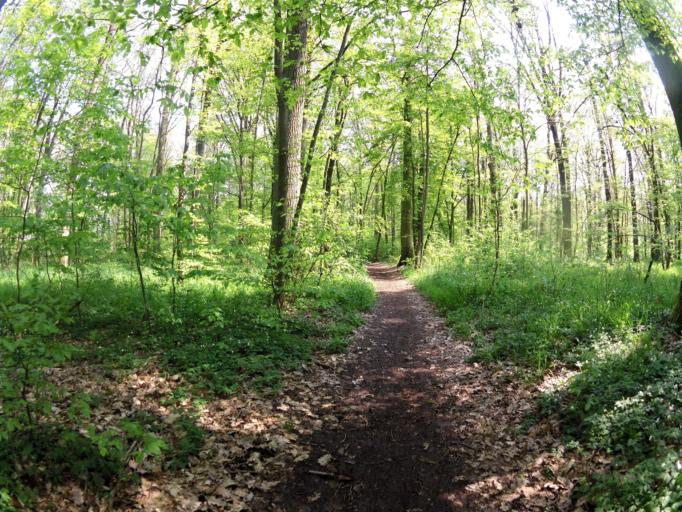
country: DE
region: Bavaria
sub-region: Regierungsbezirk Unterfranken
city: Sommerhausen
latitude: 49.7064
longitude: 10.0618
